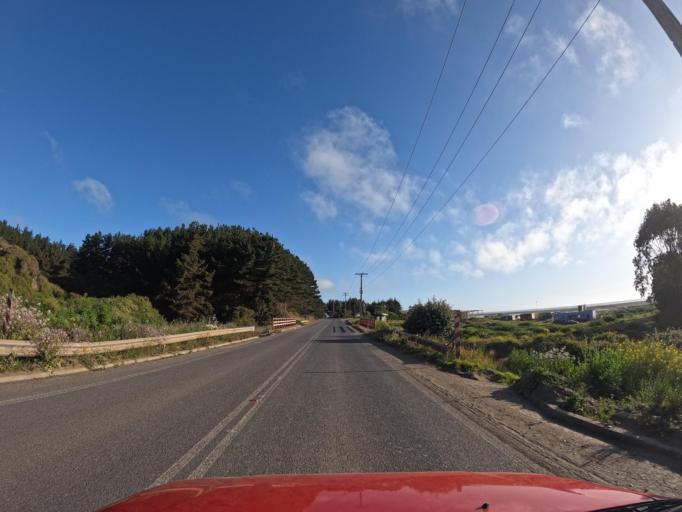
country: CL
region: Maule
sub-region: Provincia de Talca
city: Constitucion
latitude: -34.9856
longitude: -72.1785
